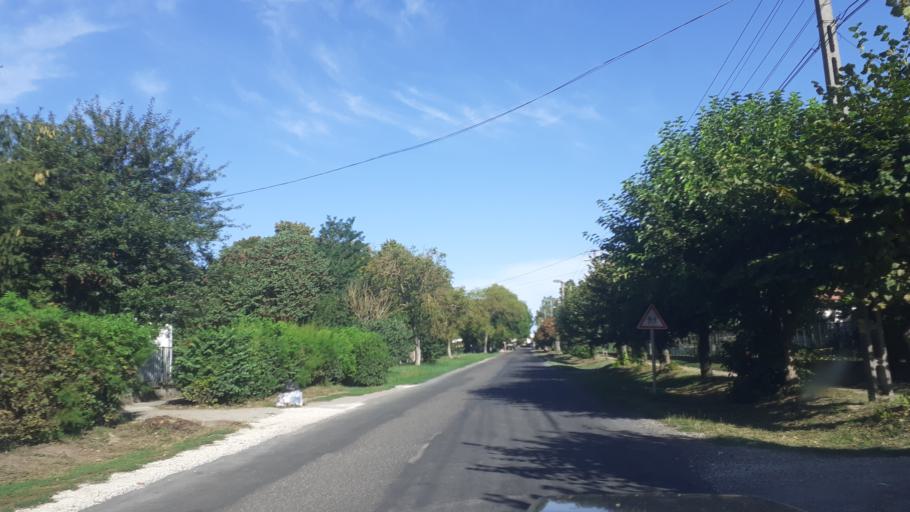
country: HU
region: Fejer
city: Ivancsa
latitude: 47.1891
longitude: 18.7963
